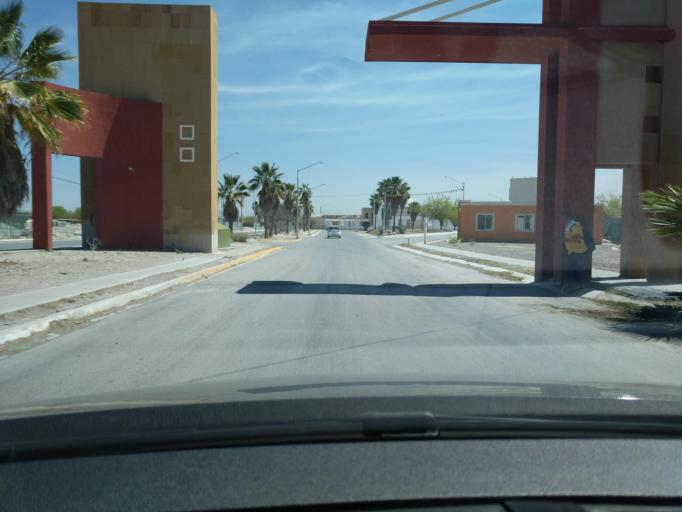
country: MX
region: Nuevo Leon
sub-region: Salinas Victoria
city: Las Torres
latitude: 25.9638
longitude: -100.3055
